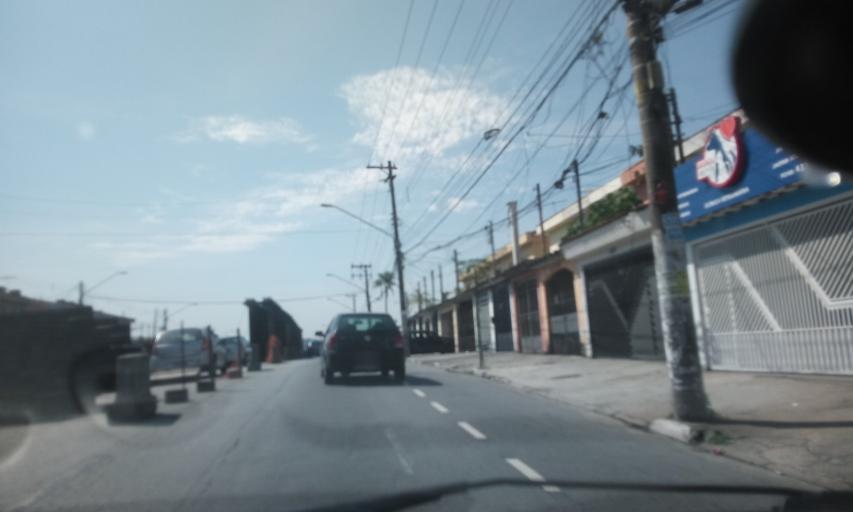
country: BR
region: Sao Paulo
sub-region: Sao Bernardo Do Campo
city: Sao Bernardo do Campo
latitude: -23.7179
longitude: -46.5355
